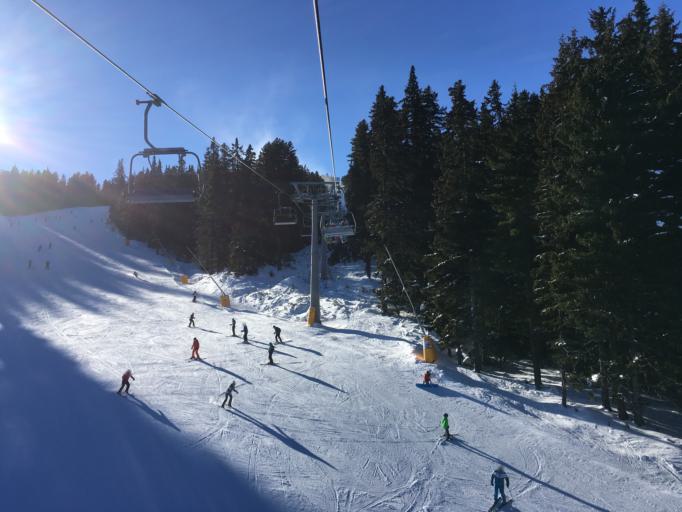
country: BG
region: Blagoevgrad
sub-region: Obshtina Bansko
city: Bansko
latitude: 41.7716
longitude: 23.4517
